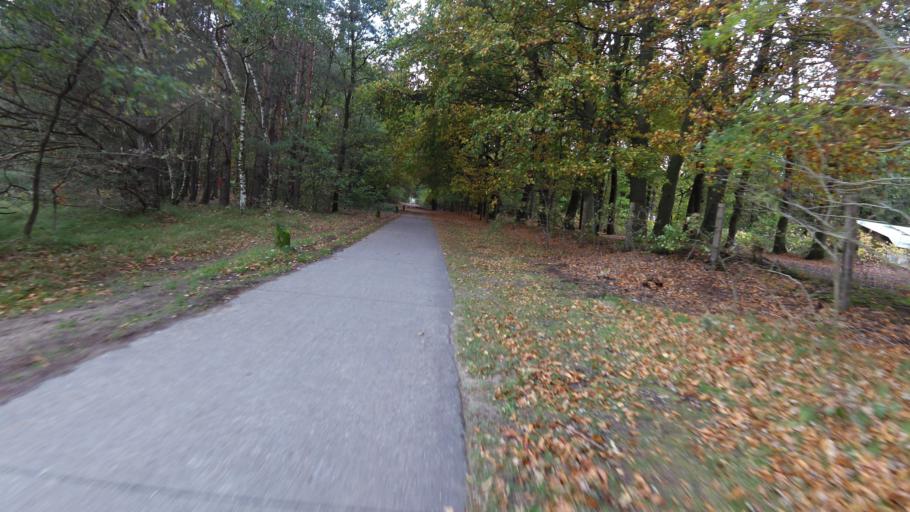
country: NL
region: Gelderland
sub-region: Gemeente Nunspeet
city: Nunspeet
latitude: 52.3302
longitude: 5.8175
